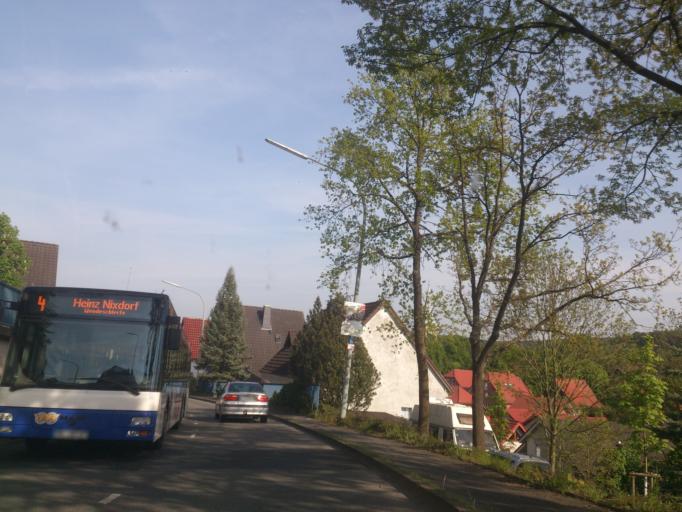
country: DE
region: North Rhine-Westphalia
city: Bad Lippspringe
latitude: 51.6971
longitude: 8.8477
